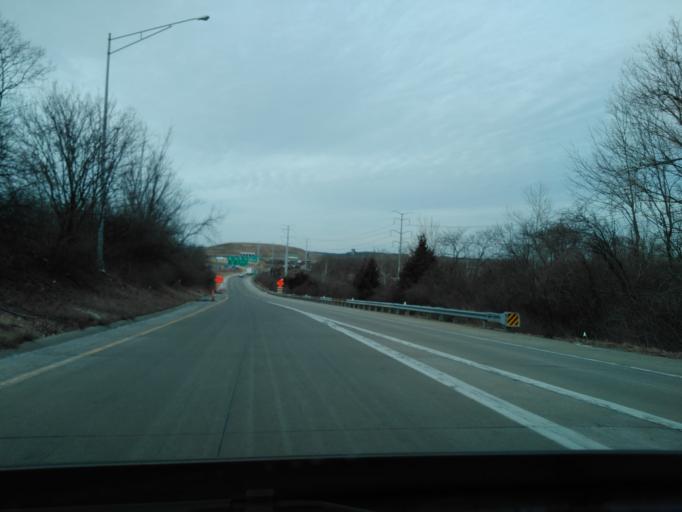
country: US
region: Missouri
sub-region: Saint Louis County
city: Valley Park
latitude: 38.5398
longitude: -90.4861
